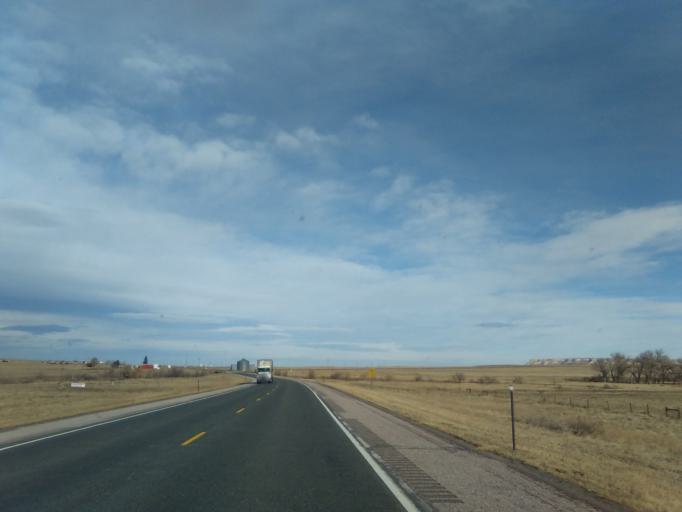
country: US
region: Wyoming
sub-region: Goshen County
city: Torrington
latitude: 41.6376
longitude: -104.2421
